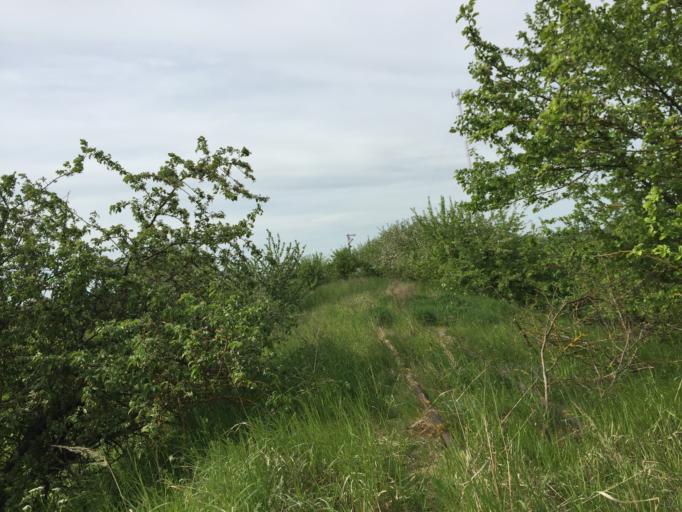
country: LT
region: Panevezys
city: Pasvalys
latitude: 56.0239
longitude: 24.1856
